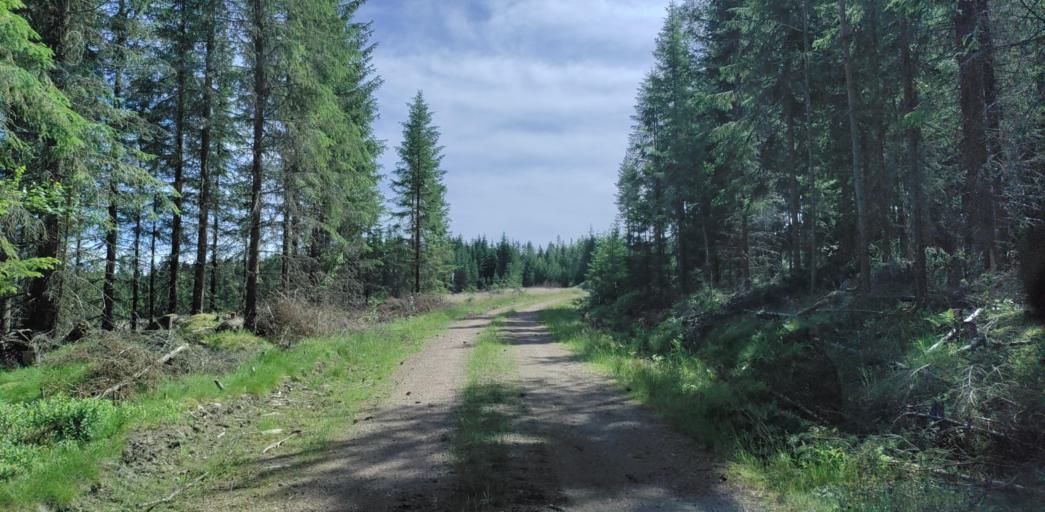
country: SE
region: Vaermland
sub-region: Hagfors Kommun
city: Ekshaerad
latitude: 60.0958
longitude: 13.3733
